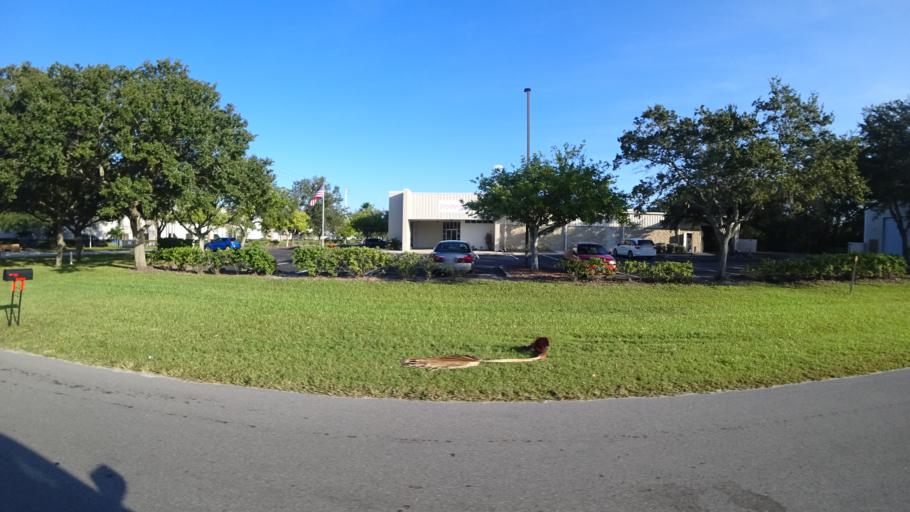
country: US
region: Florida
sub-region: Manatee County
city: Samoset
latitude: 27.4572
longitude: -82.5392
